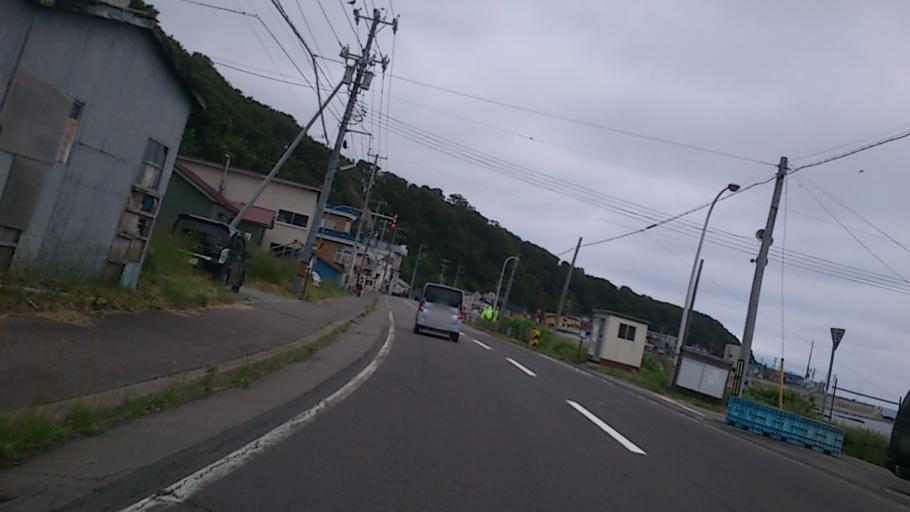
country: JP
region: Hokkaido
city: Iwanai
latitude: 42.7317
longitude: 140.0878
